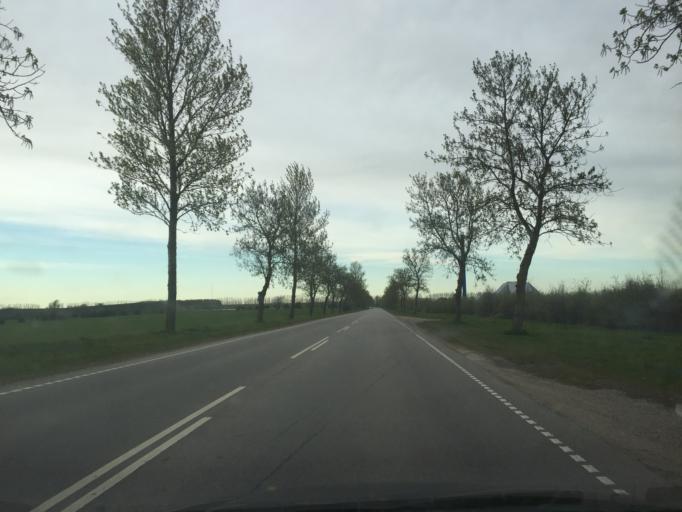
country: DK
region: Capital Region
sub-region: Hoje-Taastrup Kommune
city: Taastrup
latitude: 55.6552
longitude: 12.2527
